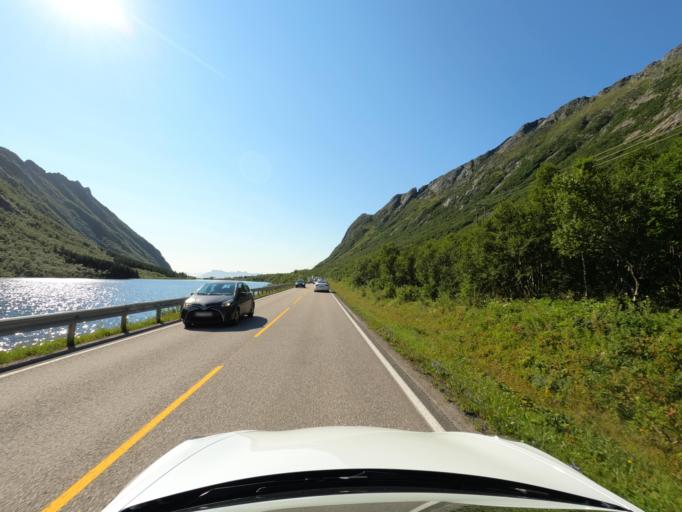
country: NO
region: Nordland
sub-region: Vagan
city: Kabelvag
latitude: 68.2084
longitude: 14.2597
